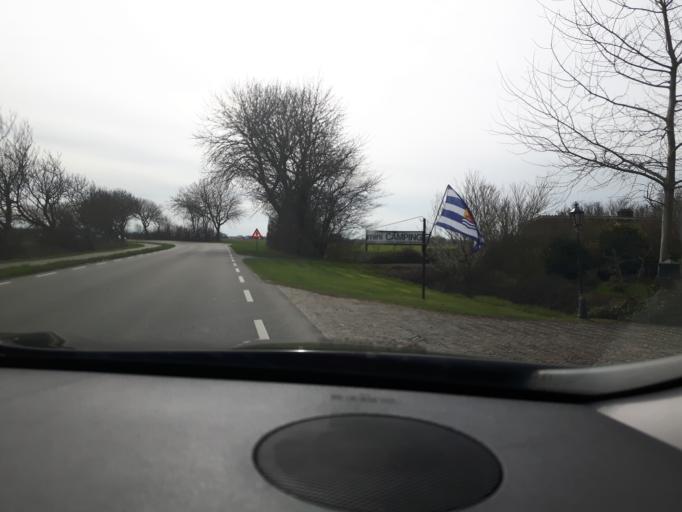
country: NL
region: Zeeland
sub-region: Gemeente Middelburg
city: Middelburg
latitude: 51.5193
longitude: 3.6003
